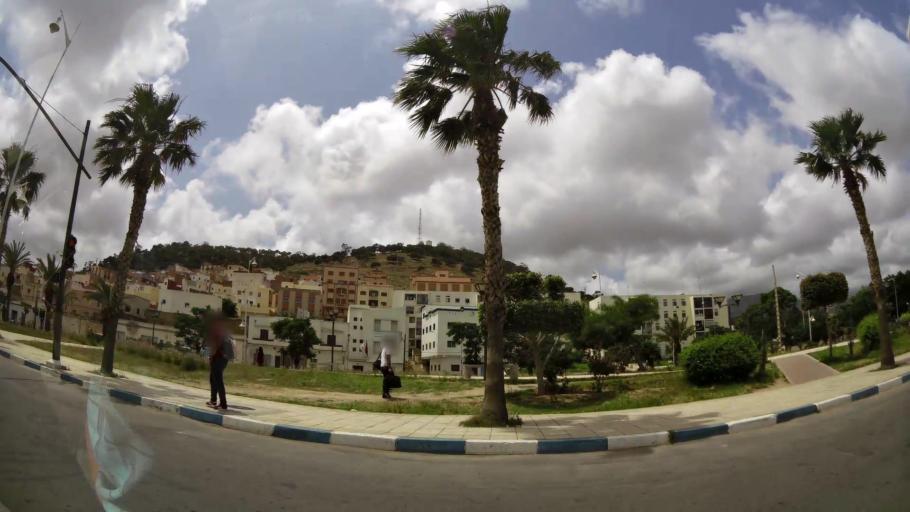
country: MA
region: Oriental
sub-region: Nador
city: Nador
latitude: 35.1830
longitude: -2.9274
